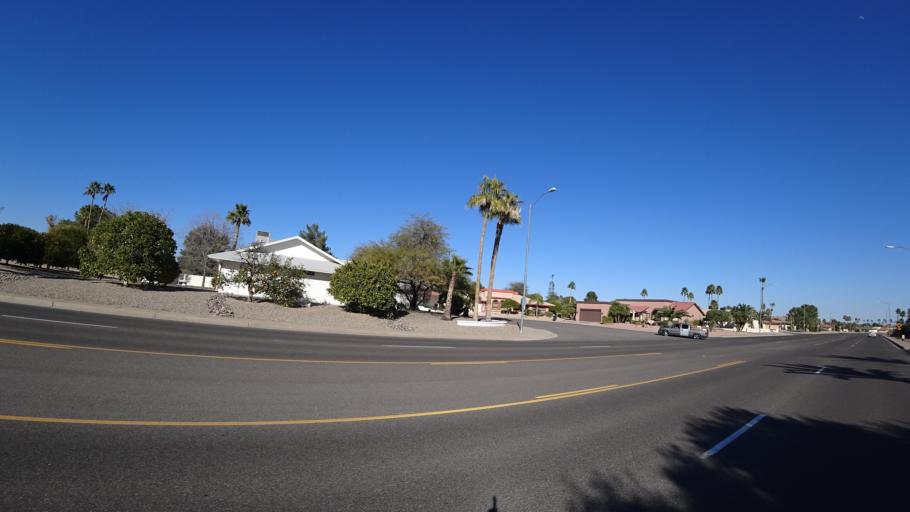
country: US
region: Arizona
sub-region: Maricopa County
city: Sun City West
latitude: 33.6788
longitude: -112.3516
